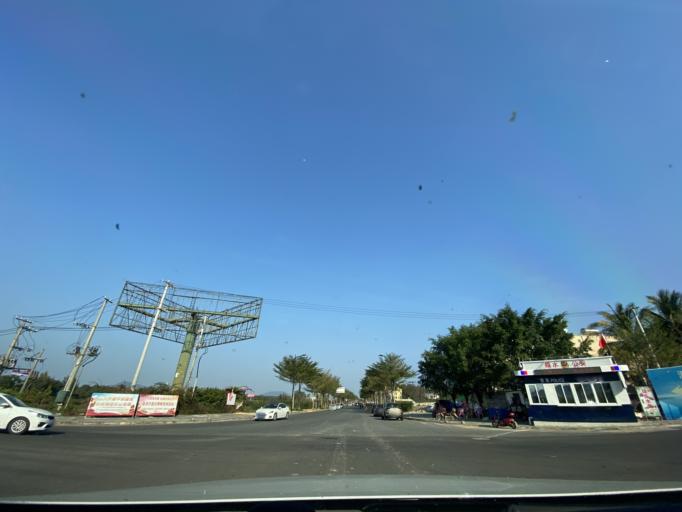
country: CN
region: Hainan
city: Haitangwan
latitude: 18.4118
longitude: 109.7876
